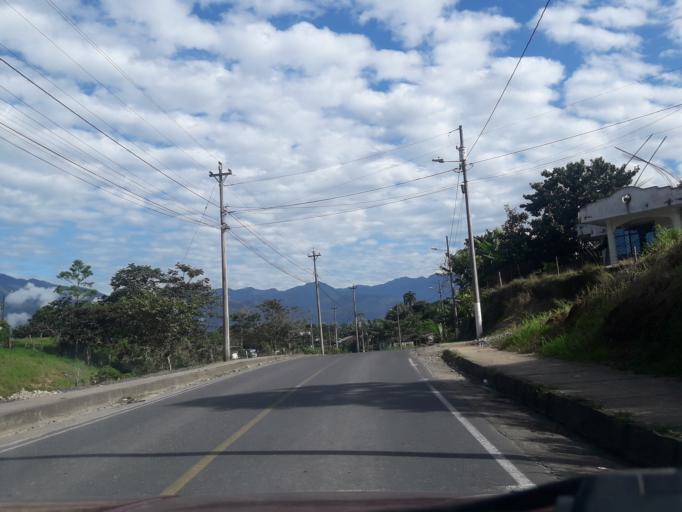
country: EC
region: Napo
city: Tena
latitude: -0.9865
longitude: -77.8357
